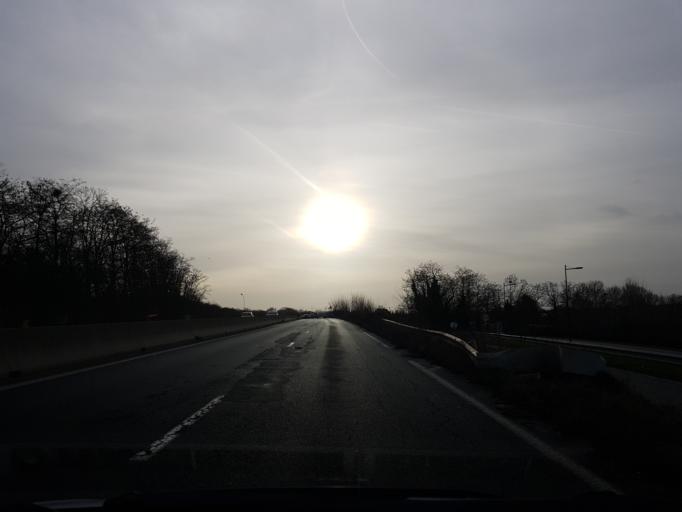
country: FR
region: Ile-de-France
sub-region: Departement de l'Essonne
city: Montgeron
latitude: 48.6948
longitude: 2.4470
